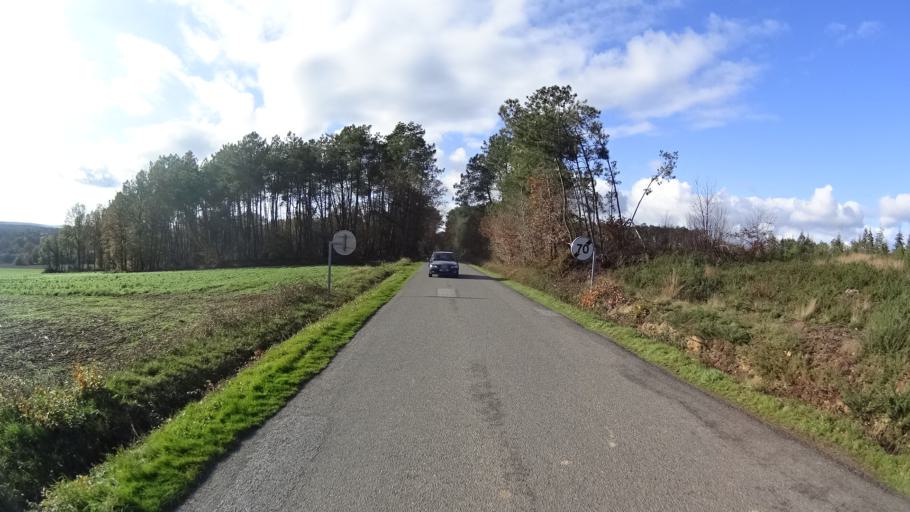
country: FR
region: Brittany
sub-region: Departement d'Ille-et-Vilaine
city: Sixt-sur-Aff
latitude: 47.8239
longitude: -2.0775
